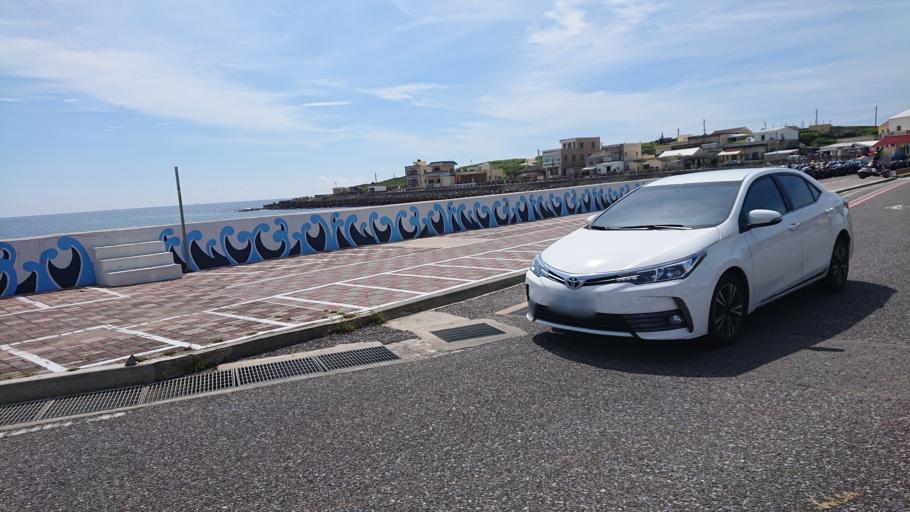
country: TW
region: Taiwan
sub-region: Penghu
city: Ma-kung
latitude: 23.6520
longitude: 119.5177
